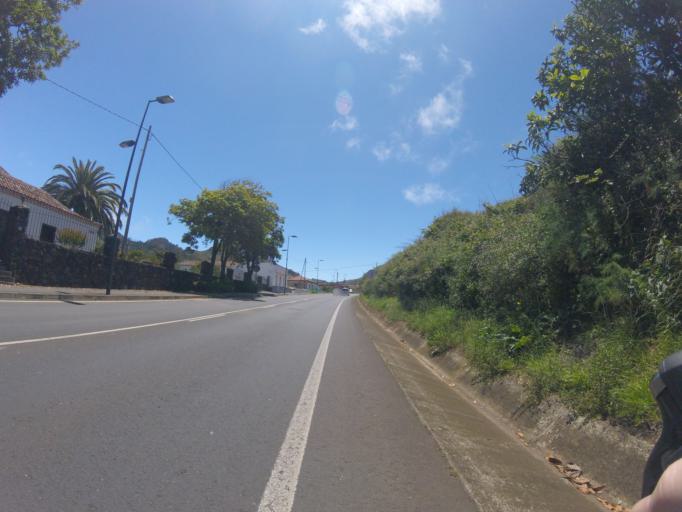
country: ES
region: Canary Islands
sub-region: Provincia de Santa Cruz de Tenerife
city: Tegueste
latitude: 28.5177
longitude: -16.3225
